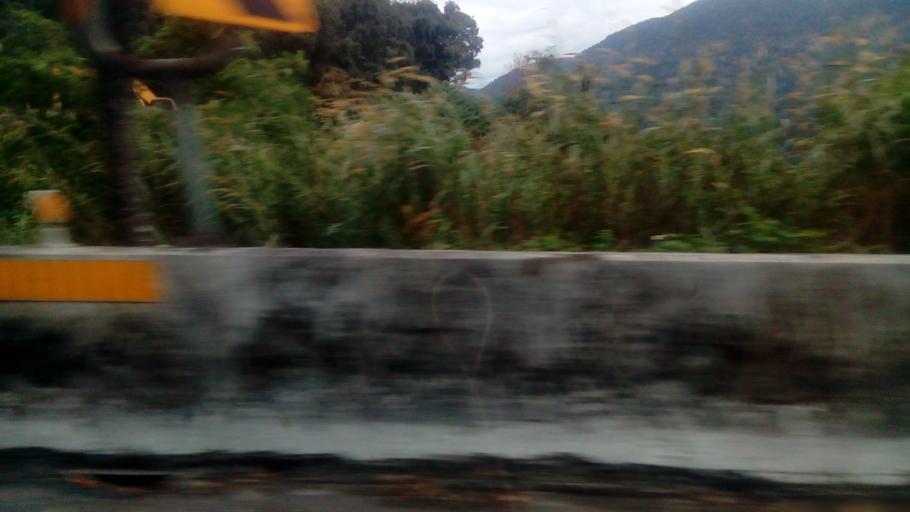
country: TW
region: Taiwan
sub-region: Yilan
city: Yilan
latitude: 24.5799
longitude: 121.4947
